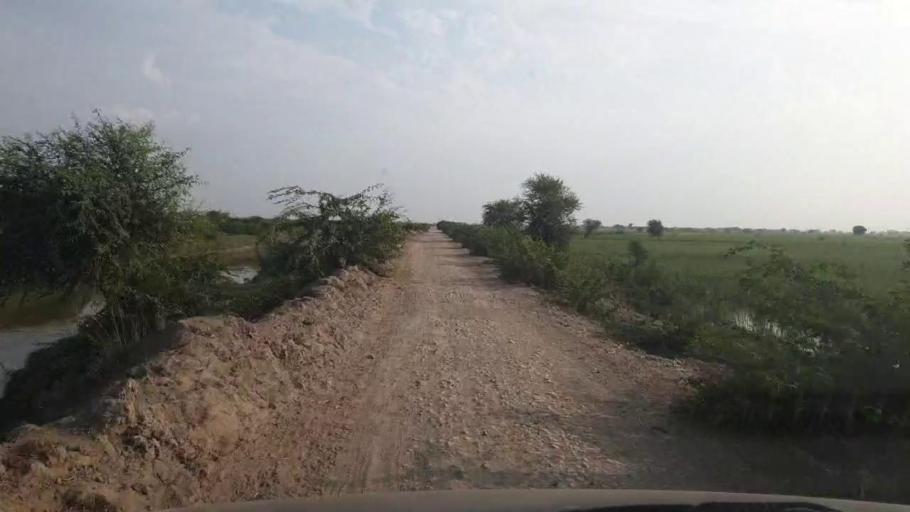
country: PK
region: Sindh
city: Badin
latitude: 24.5637
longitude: 68.6679
